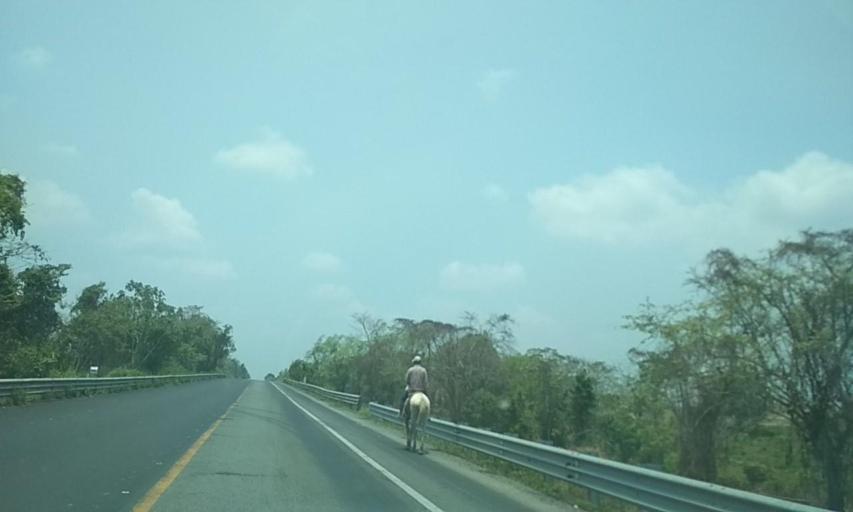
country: MX
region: Tabasco
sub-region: Huimanguillo
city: Francisco Rueda
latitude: 17.7122
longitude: -93.9425
